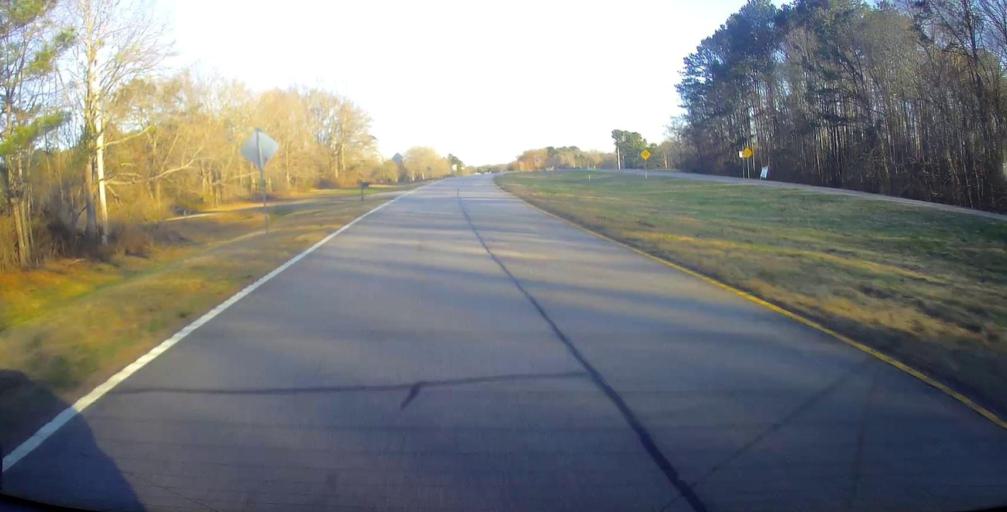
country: US
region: Georgia
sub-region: Harris County
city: Pine Mountain
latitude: 32.8585
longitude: -84.9819
